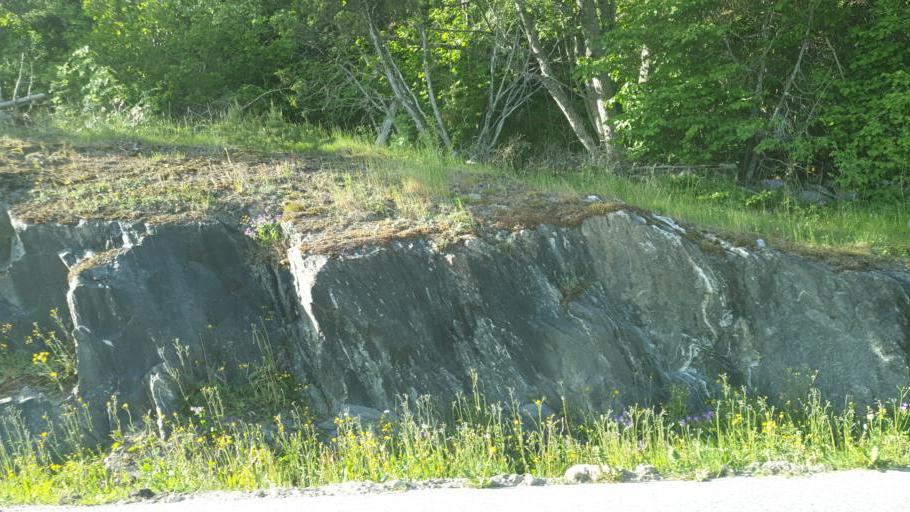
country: NO
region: Sor-Trondelag
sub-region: Rissa
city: Rissa
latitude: 63.4970
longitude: 10.1042
